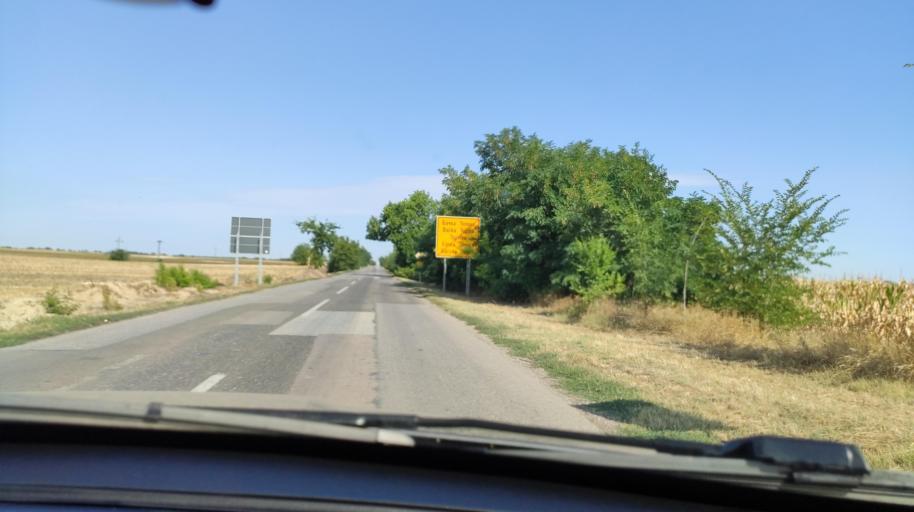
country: RS
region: Autonomna Pokrajina Vojvodina
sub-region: Severnobacki Okrug
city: Backa Topola
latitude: 45.8161
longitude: 19.6160
